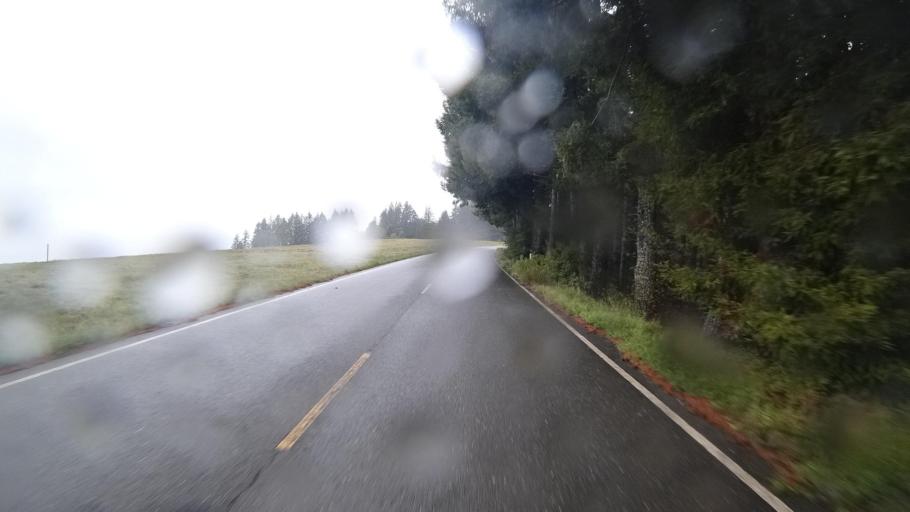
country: US
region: California
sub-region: Humboldt County
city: Westhaven-Moonstone
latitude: 41.1941
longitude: -123.9403
